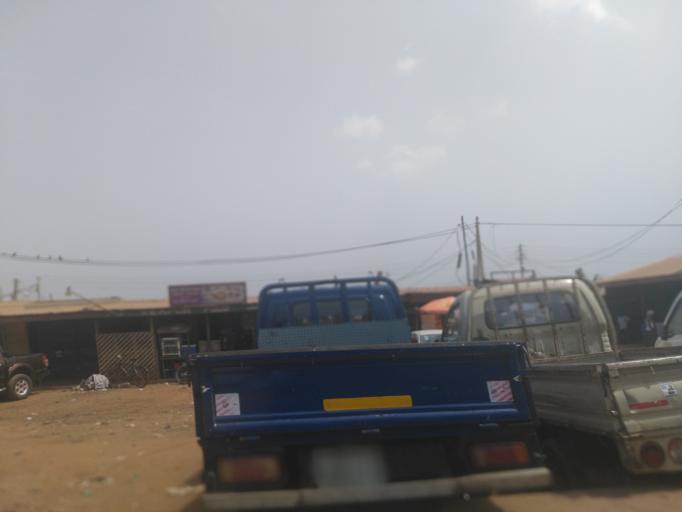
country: GH
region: Greater Accra
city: Tema
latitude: 5.6969
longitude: -0.0138
